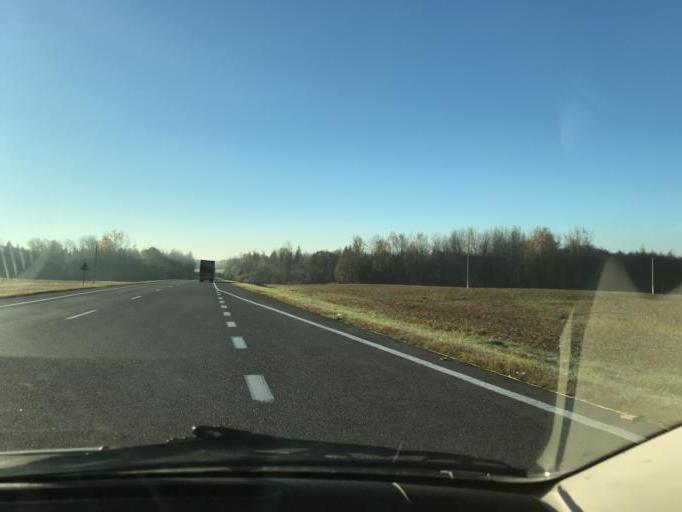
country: BY
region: Vitebsk
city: Vitebsk
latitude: 54.9966
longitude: 30.3387
